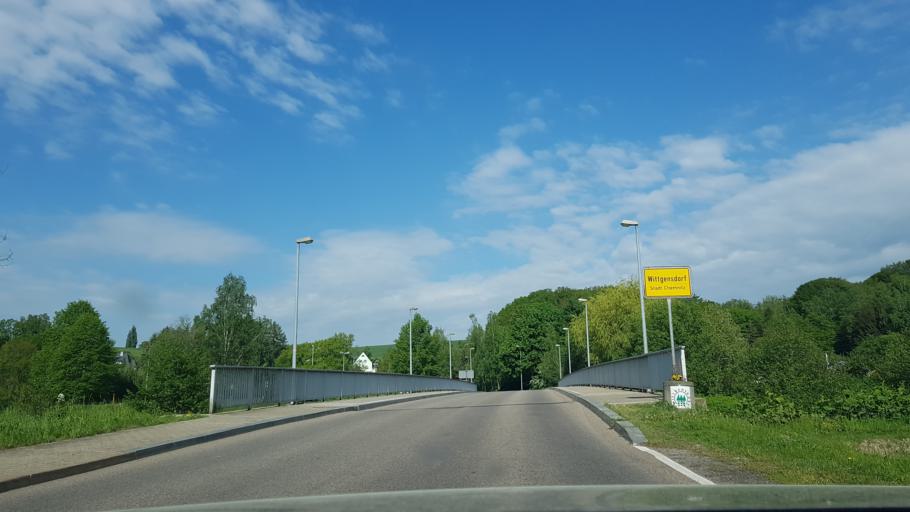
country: DE
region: Saxony
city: Wittgensdorf
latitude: 50.8932
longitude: 12.8947
